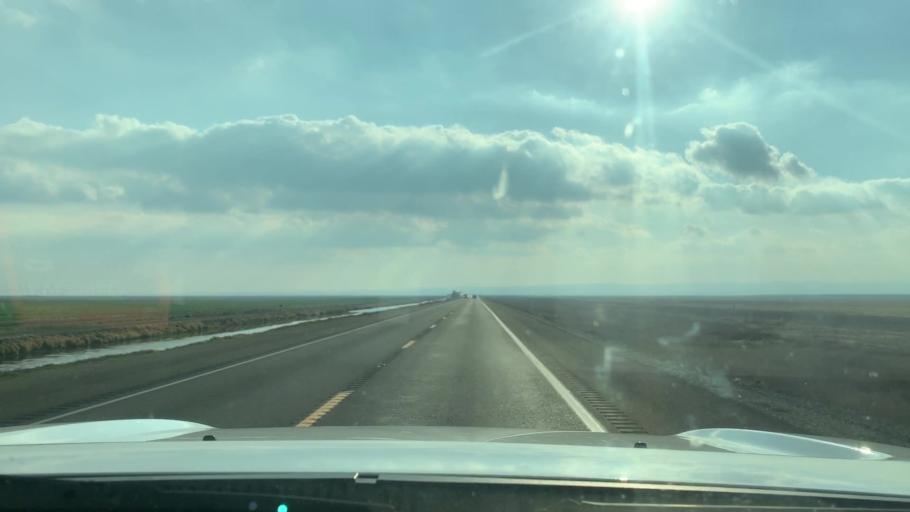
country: US
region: California
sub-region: Kings County
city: Stratford
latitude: 36.1145
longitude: -119.8978
